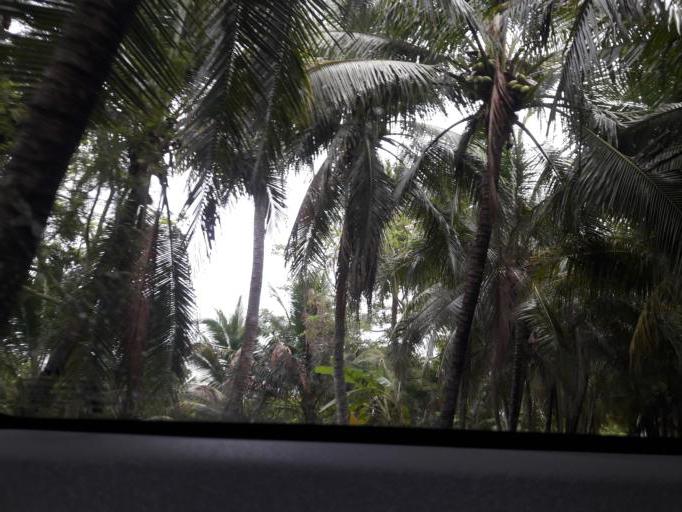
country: TH
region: Ratchaburi
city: Damnoen Saduak
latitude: 13.5738
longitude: 99.9867
